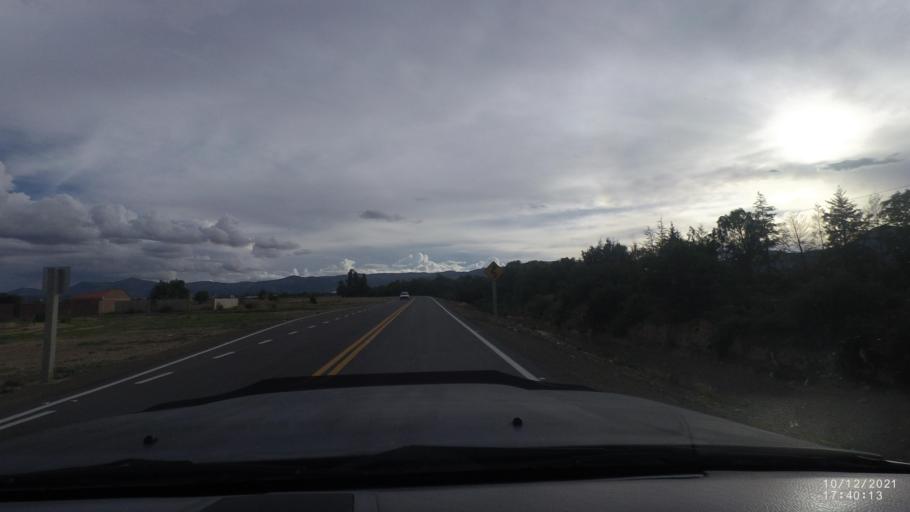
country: BO
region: Cochabamba
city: Tarata
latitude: -17.5842
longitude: -66.0192
